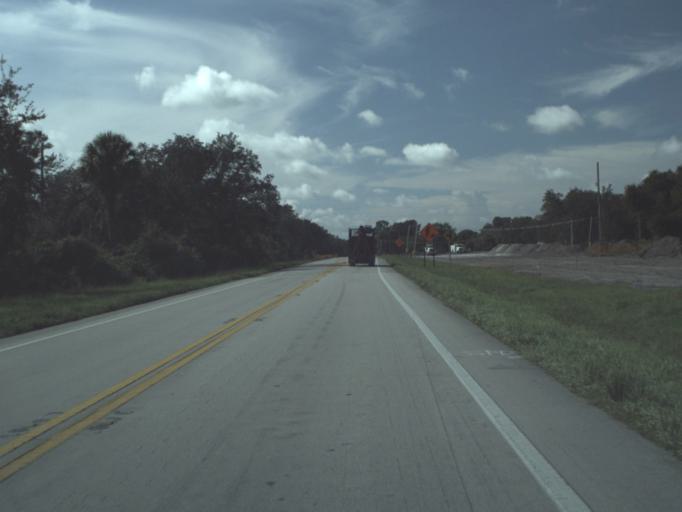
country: US
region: Florida
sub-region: Okeechobee County
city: Cypress Quarters
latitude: 27.5265
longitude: -80.8070
